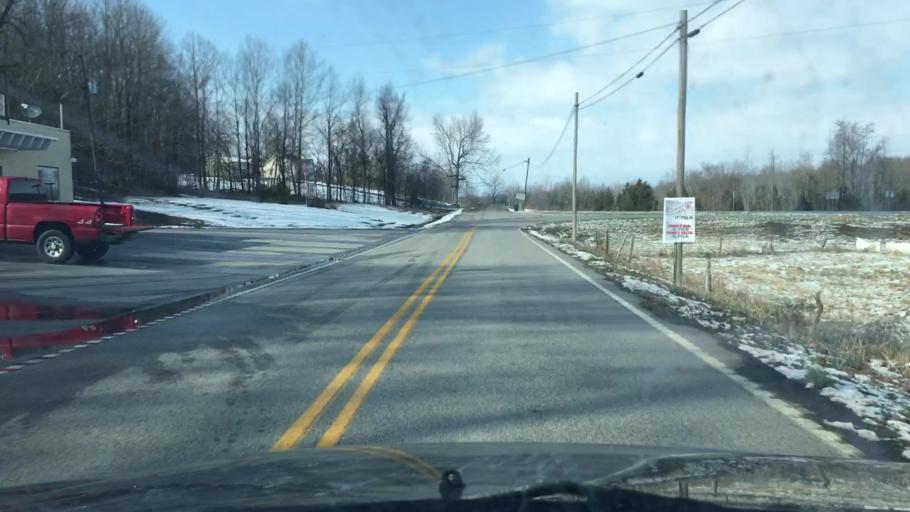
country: US
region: Kentucky
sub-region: Marion County
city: Lebanon
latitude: 37.5258
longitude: -85.3029
